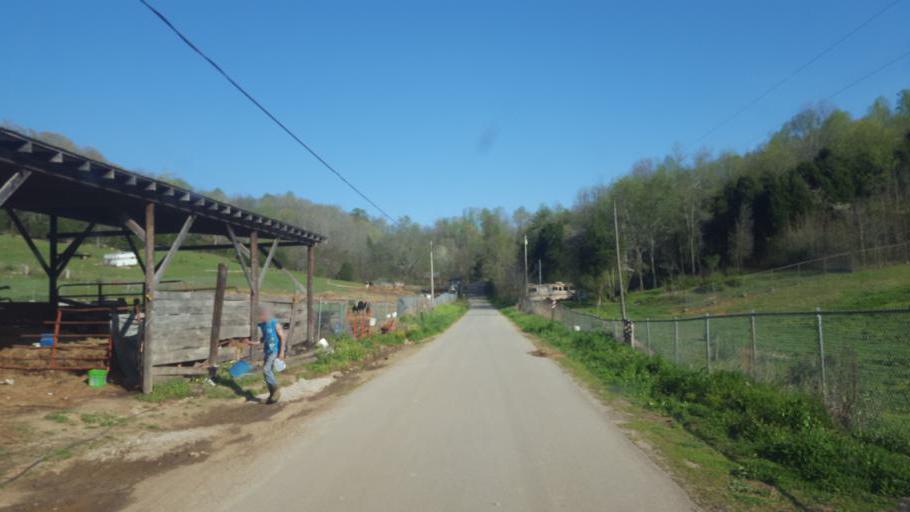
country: US
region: Kentucky
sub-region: Barren County
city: Cave City
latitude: 37.1776
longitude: -86.0047
